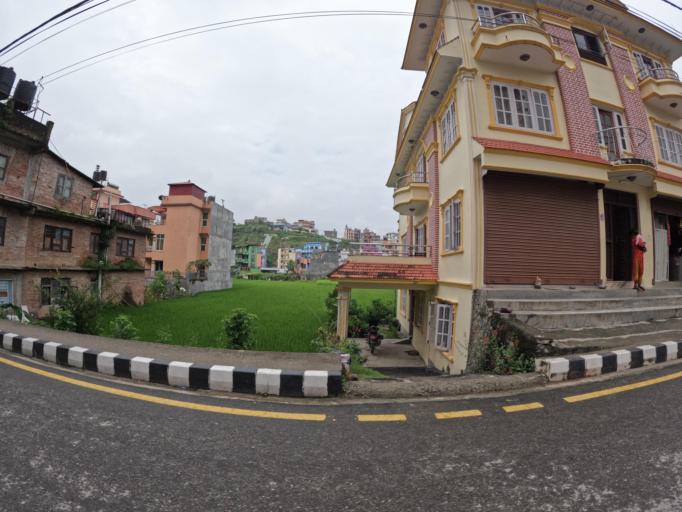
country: NP
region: Central Region
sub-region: Bagmati Zone
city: Kathmandu
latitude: 27.7550
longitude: 85.3255
